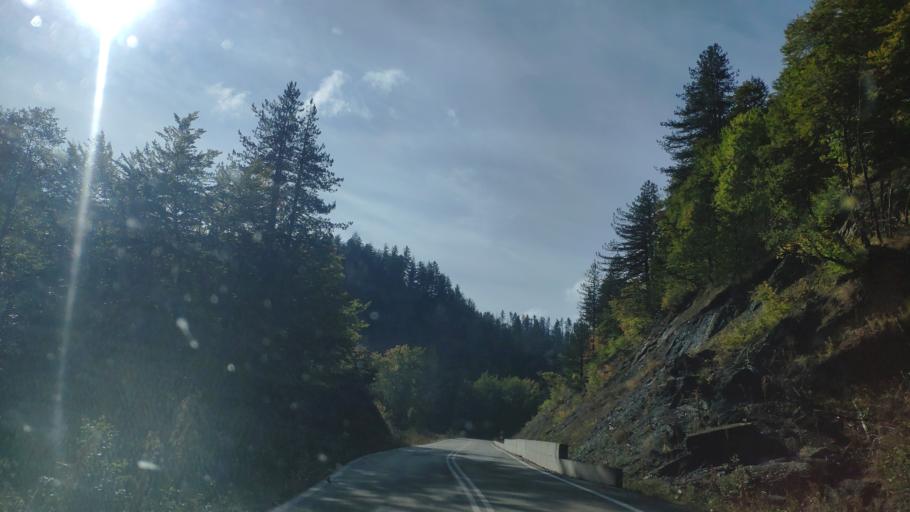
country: GR
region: West Macedonia
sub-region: Nomos Kastorias
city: Nestorio
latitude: 40.3785
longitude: 20.9411
